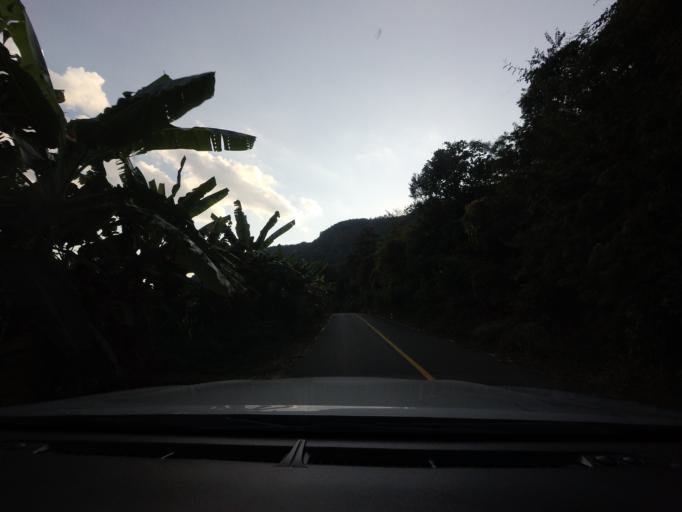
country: TH
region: Chiang Mai
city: Chai Prakan
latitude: 19.5488
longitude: 99.1613
